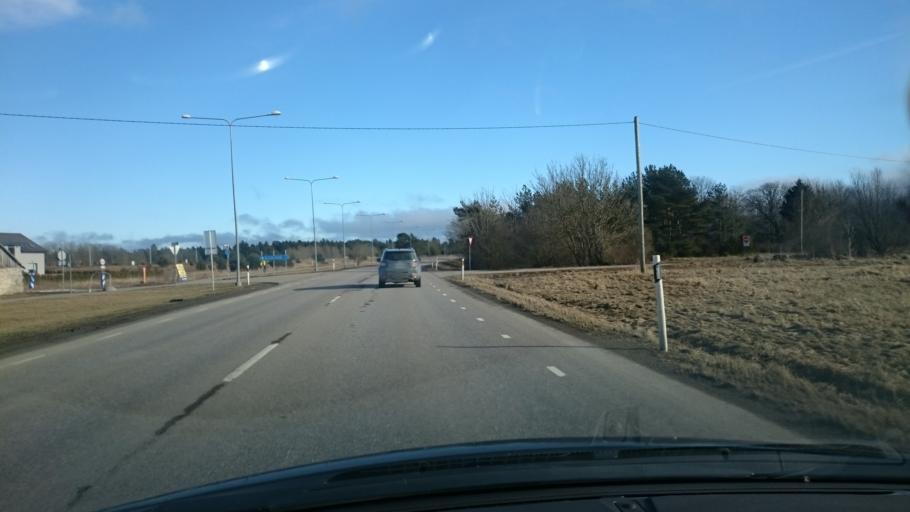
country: EE
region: Harju
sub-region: Harku vald
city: Tabasalu
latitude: 59.4424
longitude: 24.4897
